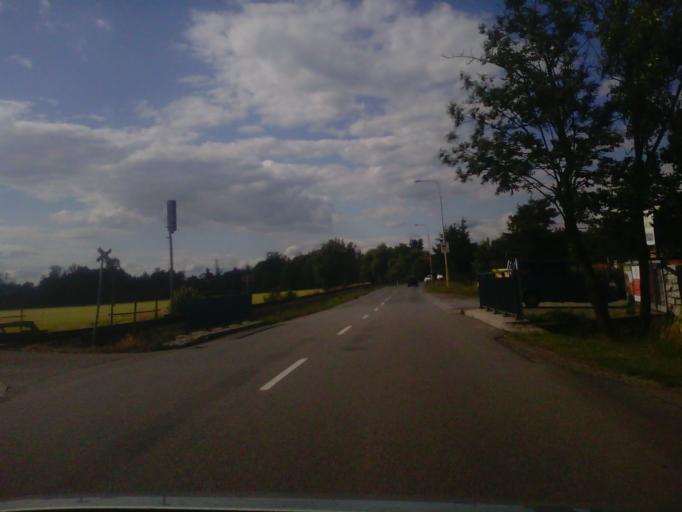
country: CZ
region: Olomoucky
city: Litovel
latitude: 49.6964
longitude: 17.0716
